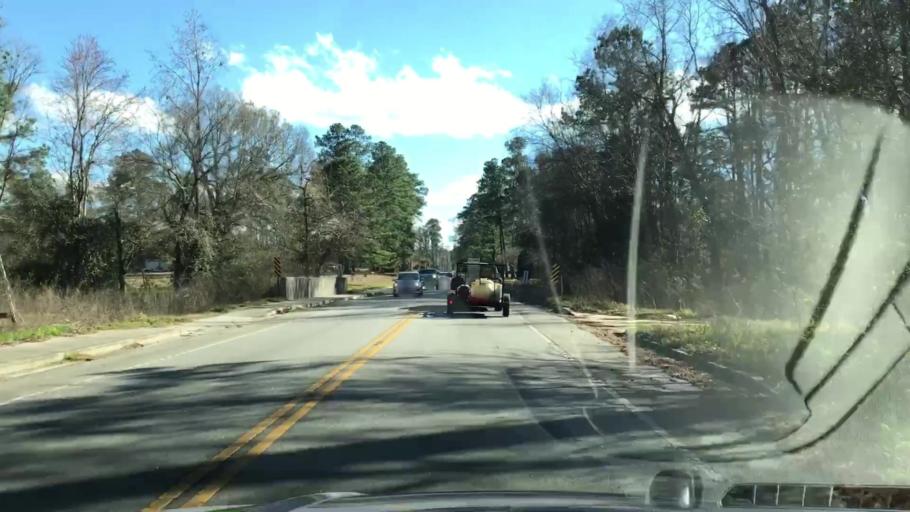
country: US
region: South Carolina
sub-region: Dorchester County
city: Summerville
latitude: 33.0276
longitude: -80.2438
